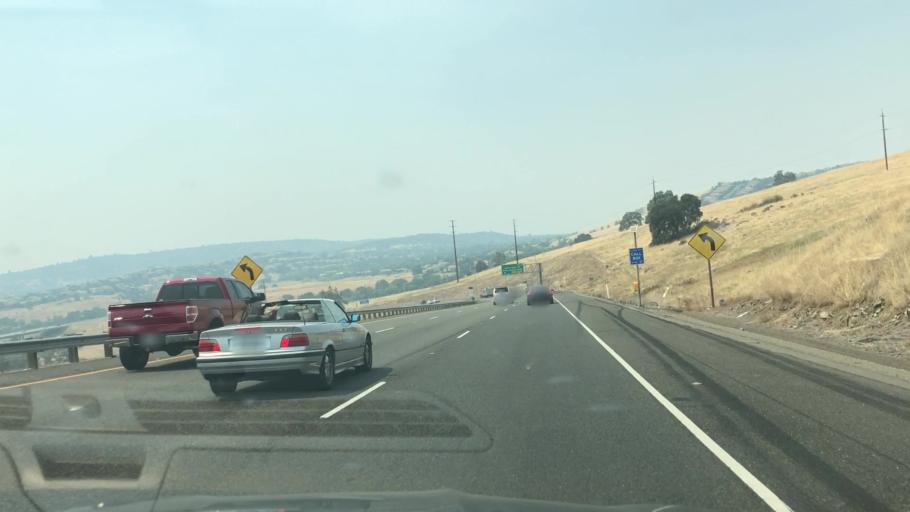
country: US
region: California
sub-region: El Dorado County
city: El Dorado Hills
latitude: 38.6560
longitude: -121.0429
